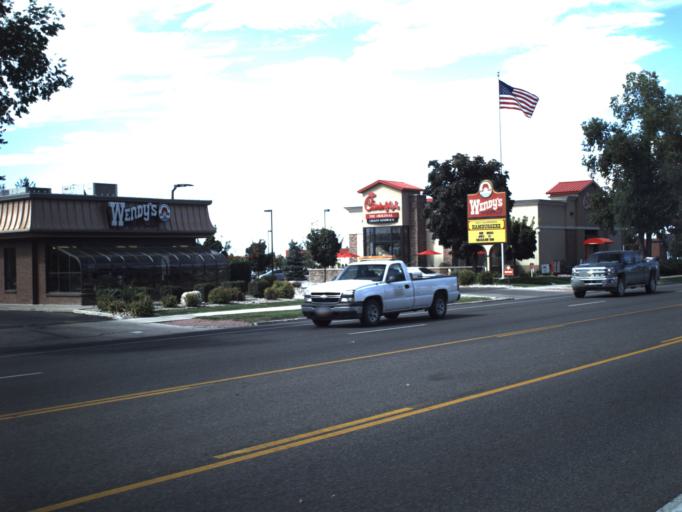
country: US
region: Utah
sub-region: Cache County
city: Logan
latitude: 41.7556
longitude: -111.8343
